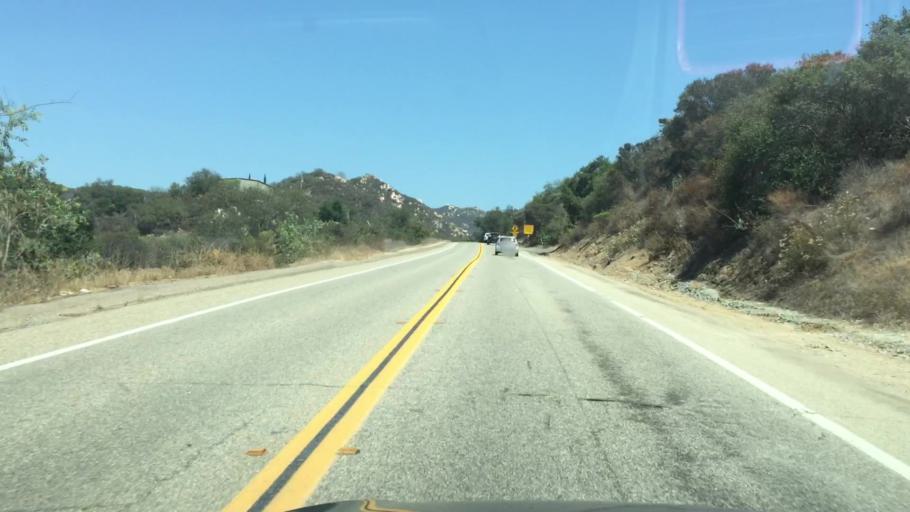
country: US
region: California
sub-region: San Diego County
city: Jamul
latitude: 32.7330
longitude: -116.8232
